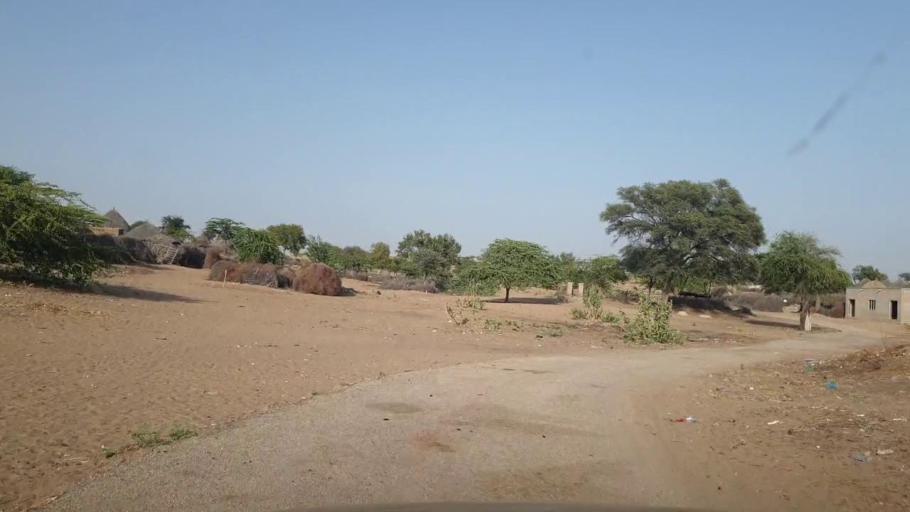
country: PK
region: Sindh
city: Islamkot
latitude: 25.1227
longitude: 70.4233
